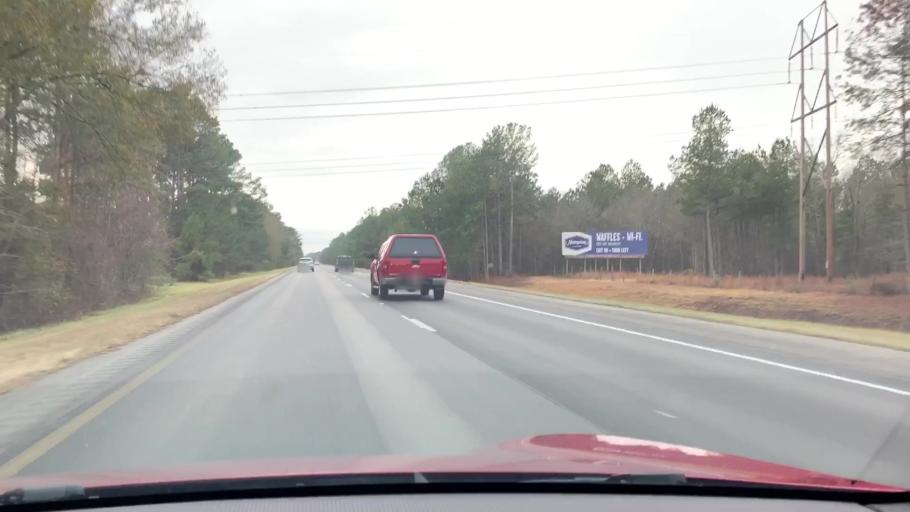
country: US
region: South Carolina
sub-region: Clarendon County
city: Manning
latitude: 33.6272
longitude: -80.2972
